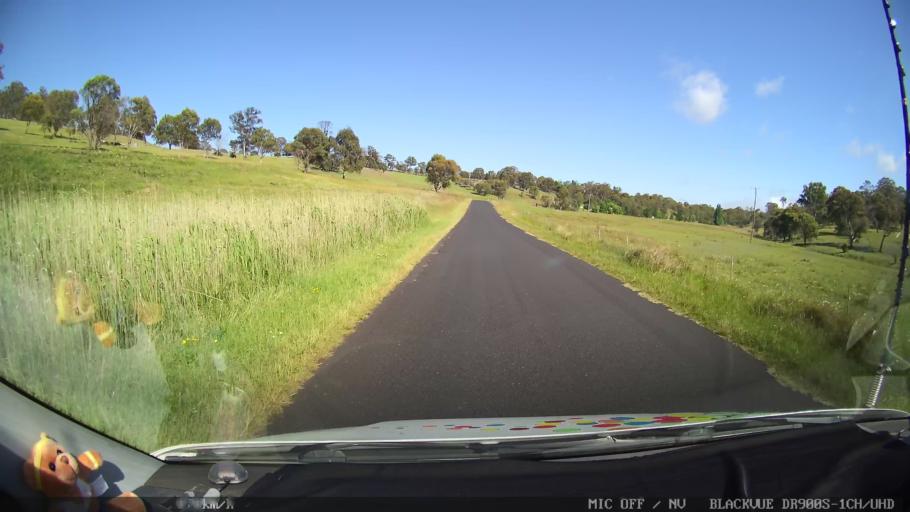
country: AU
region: New South Wales
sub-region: Guyra
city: Guyra
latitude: -30.1152
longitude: 151.6861
